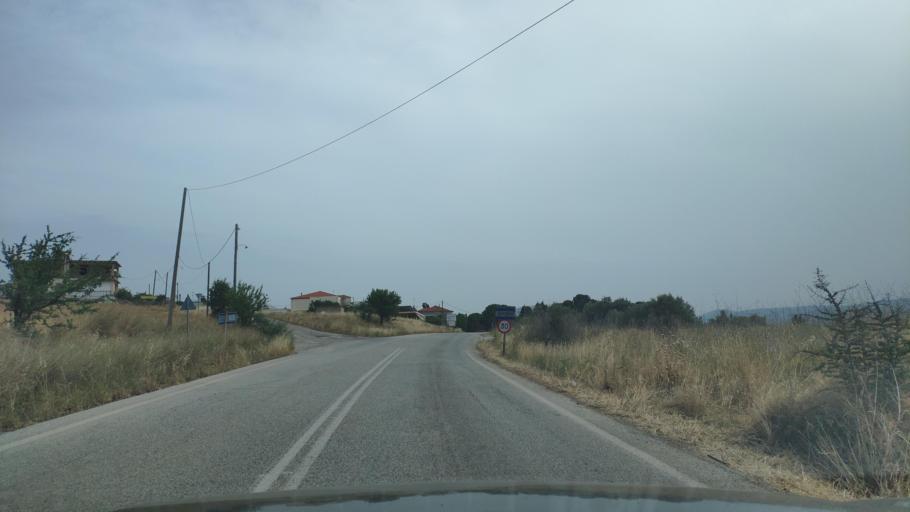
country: GR
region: Peloponnese
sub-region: Nomos Argolidos
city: Palaia Epidavros
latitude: 37.5673
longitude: 23.1497
